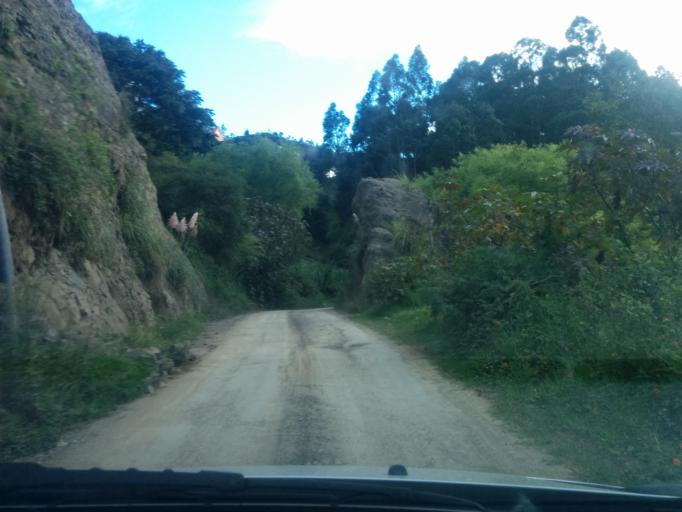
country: EC
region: Azuay
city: Cuenca
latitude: -2.8834
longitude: -78.9479
